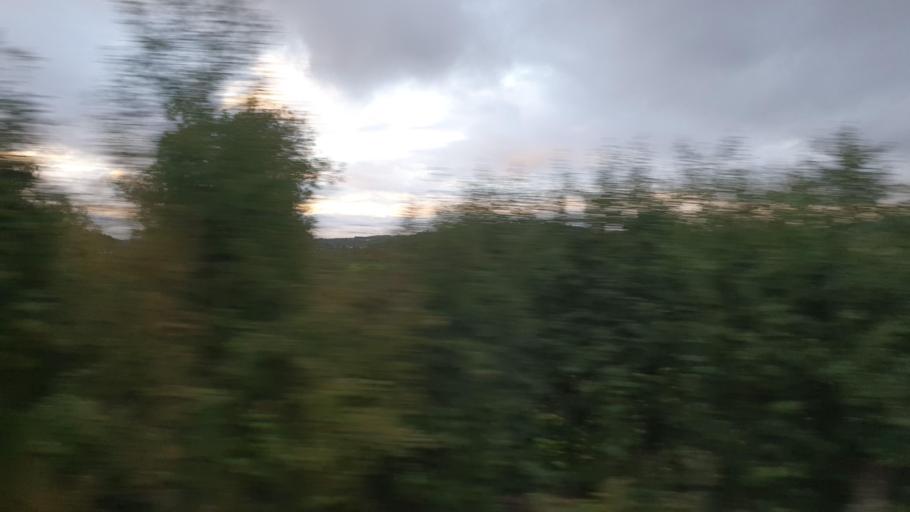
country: NO
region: Nord-Trondelag
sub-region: Levanger
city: Skogn
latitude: 63.6772
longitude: 11.1419
